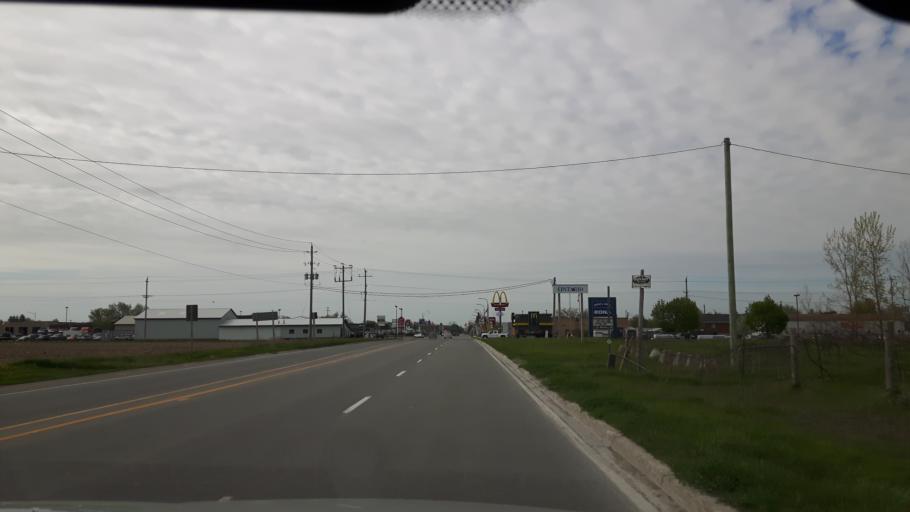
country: CA
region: Ontario
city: South Huron
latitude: 43.3650
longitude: -81.4843
